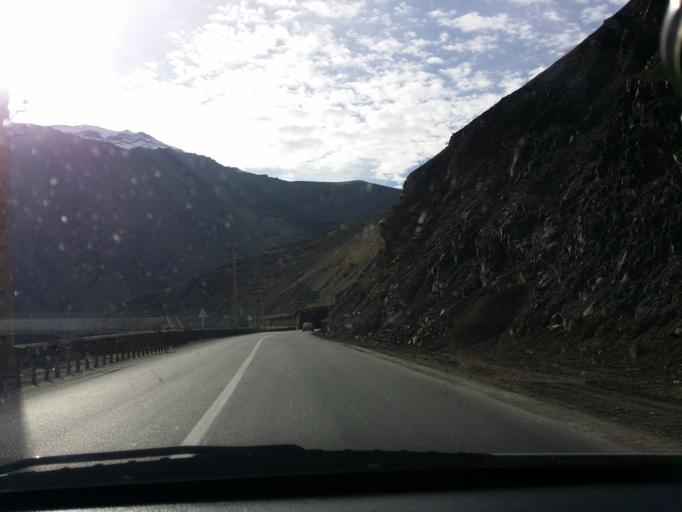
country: IR
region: Alborz
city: Karaj
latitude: 36.0103
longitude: 51.1232
